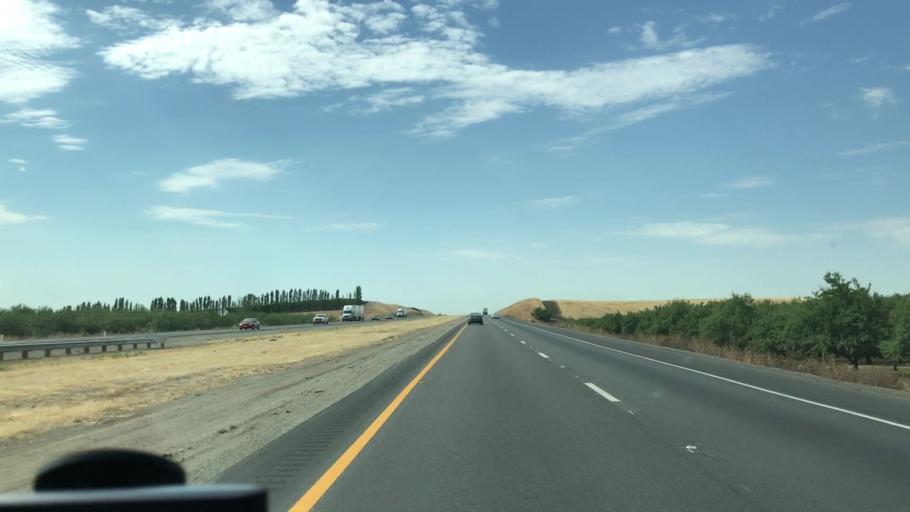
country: US
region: California
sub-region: Stanislaus County
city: Patterson
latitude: 37.3734
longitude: -121.1258
